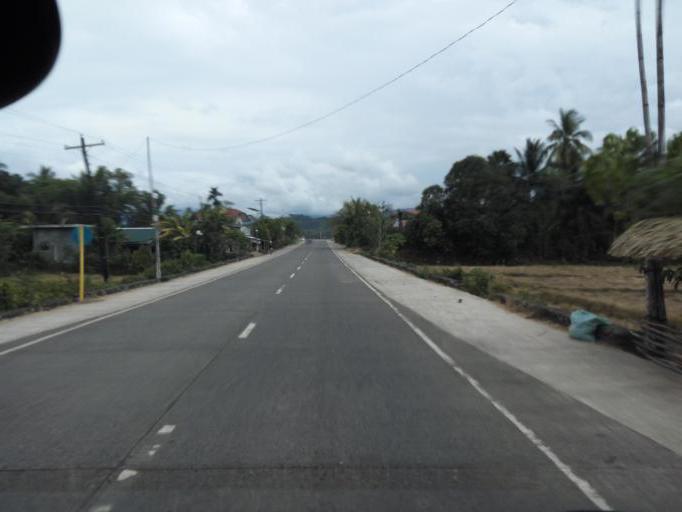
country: PH
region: Cagayan Valley
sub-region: Province of Cagayan
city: Gonzaga
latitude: 18.2437
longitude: 121.9601
